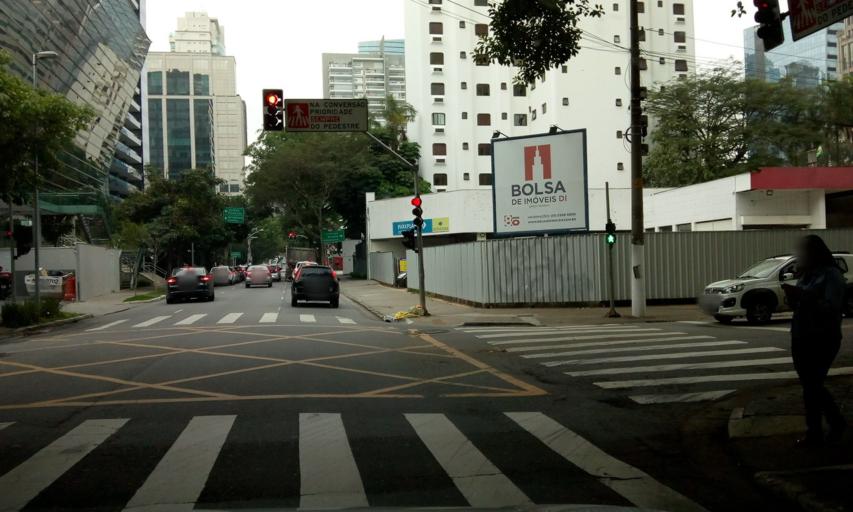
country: BR
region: Sao Paulo
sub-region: Sao Paulo
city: Sao Paulo
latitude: -23.5878
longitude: -46.6835
